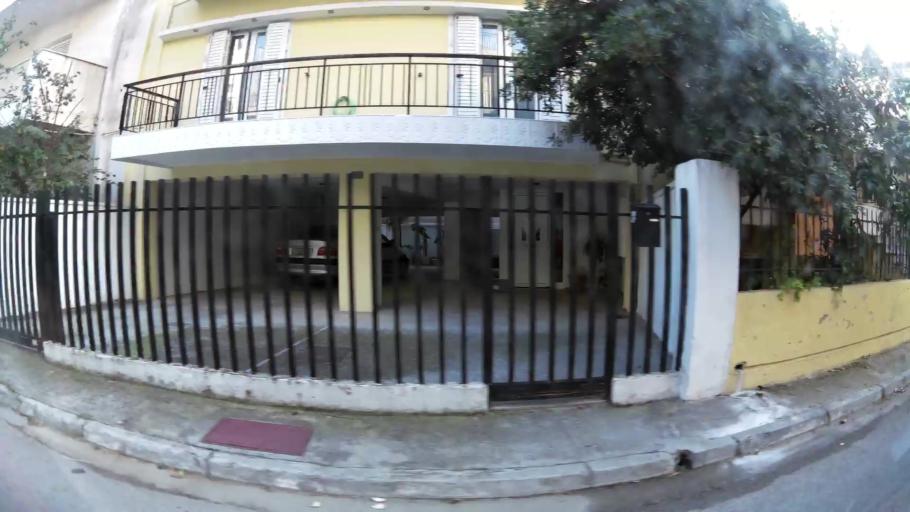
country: GR
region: Attica
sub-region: Nomarchia Anatolikis Attikis
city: Acharnes
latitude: 38.0853
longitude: 23.7414
